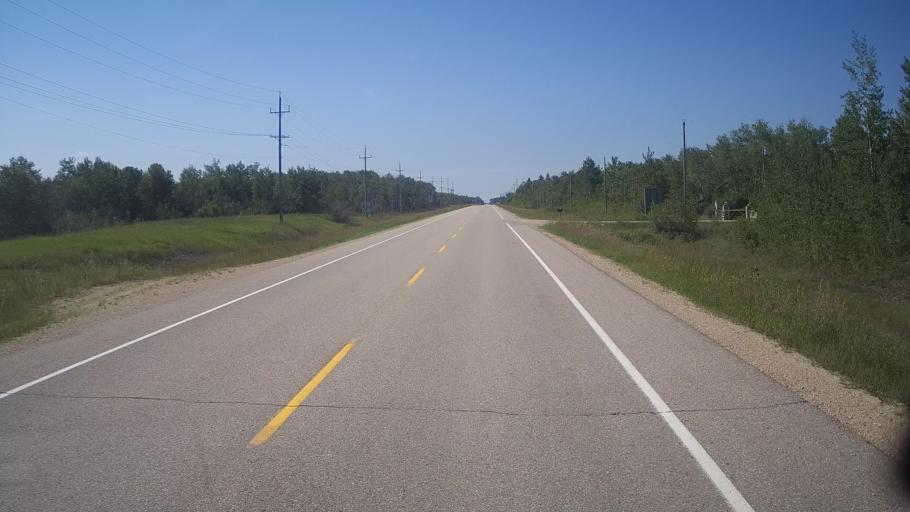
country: CA
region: Manitoba
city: La Broquerie
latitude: 49.6757
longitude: -96.4569
